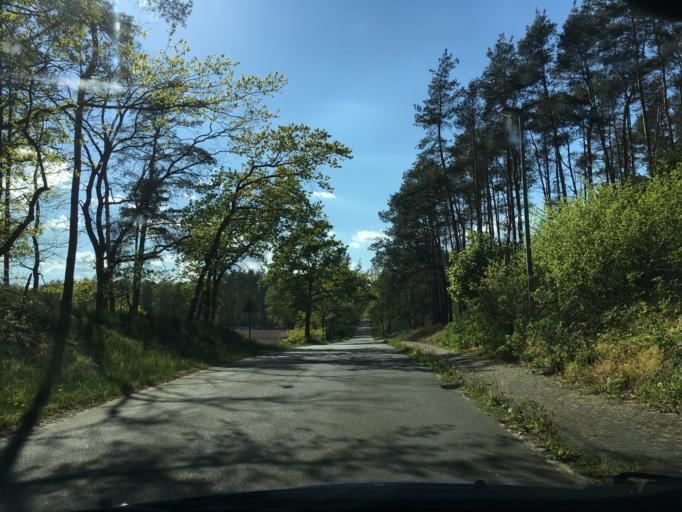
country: DE
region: Lower Saxony
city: Gartow
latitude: 53.0566
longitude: 11.4516
